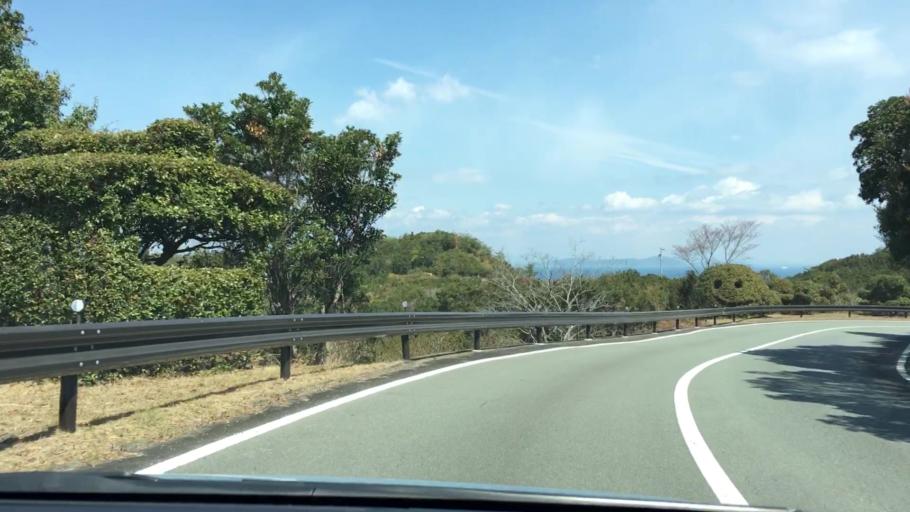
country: JP
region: Mie
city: Toba
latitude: 34.4279
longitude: 136.9106
